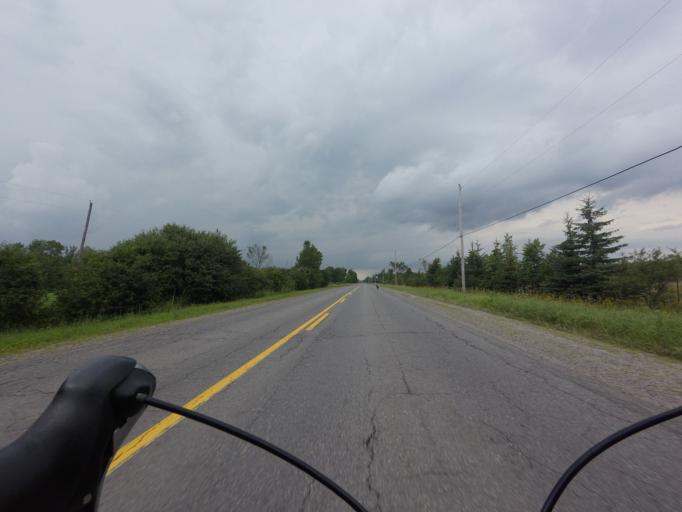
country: CA
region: Ontario
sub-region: Lanark County
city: Smiths Falls
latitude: 44.8667
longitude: -75.8088
